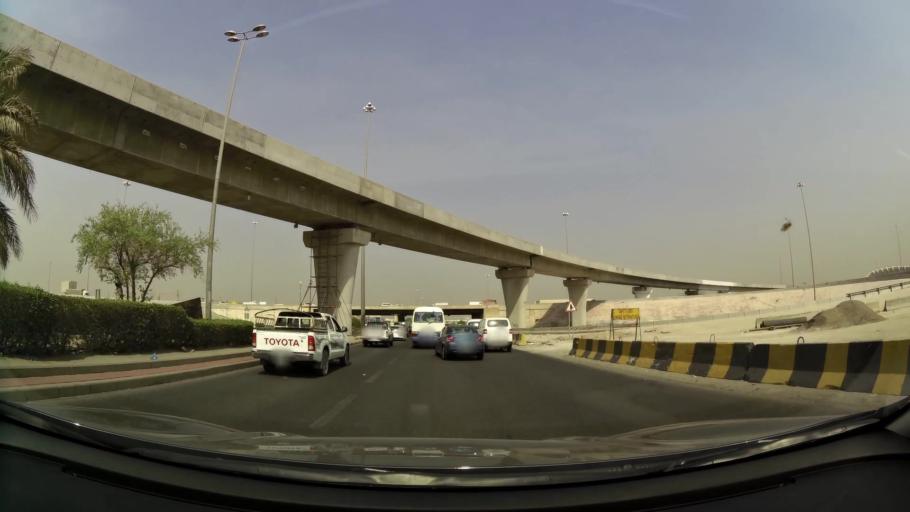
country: KW
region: Al Asimah
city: Ar Rabiyah
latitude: 29.2661
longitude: 47.9081
